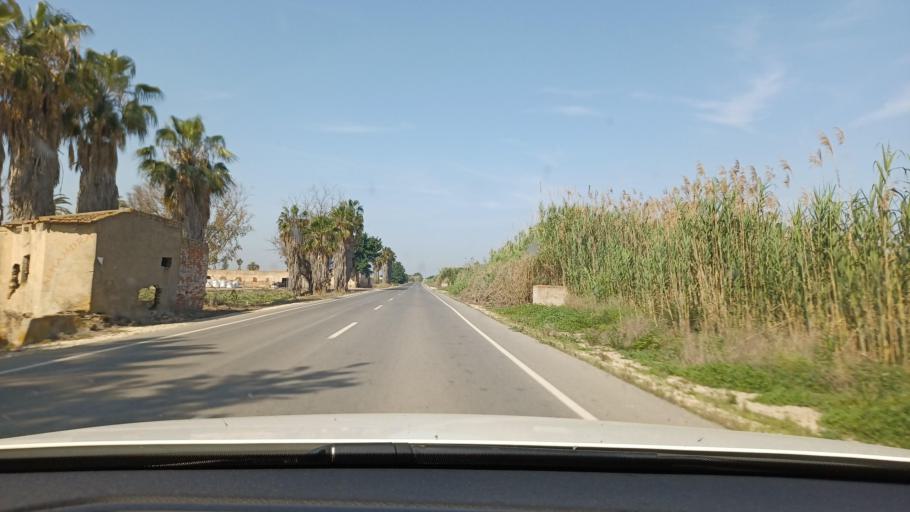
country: ES
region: Valencia
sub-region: Provincia de Alicante
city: Daya Vieja
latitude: 38.1476
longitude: -0.7224
